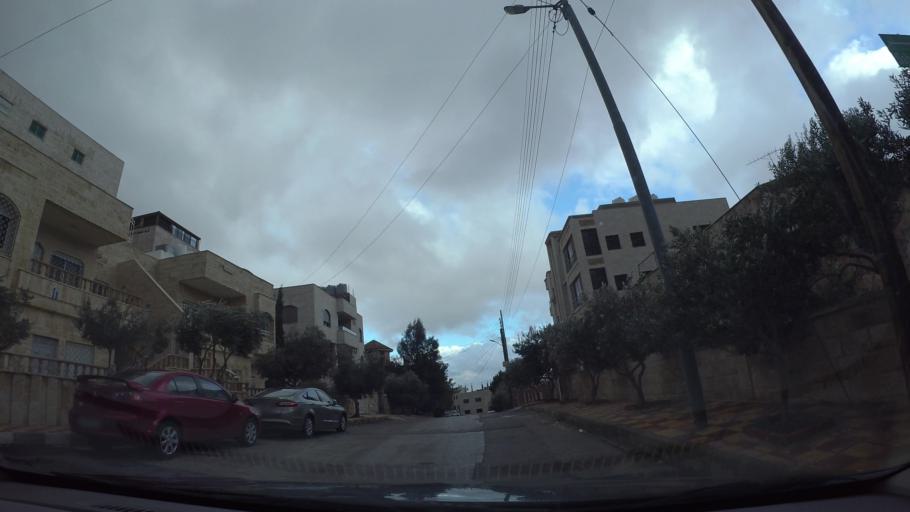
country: JO
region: Amman
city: Amman
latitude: 32.0058
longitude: 35.9292
